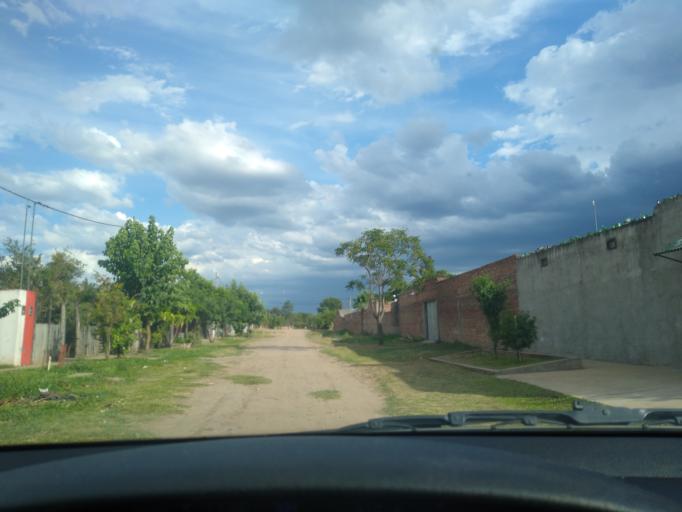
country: AR
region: Chaco
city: Fontana
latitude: -27.4048
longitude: -59.0472
